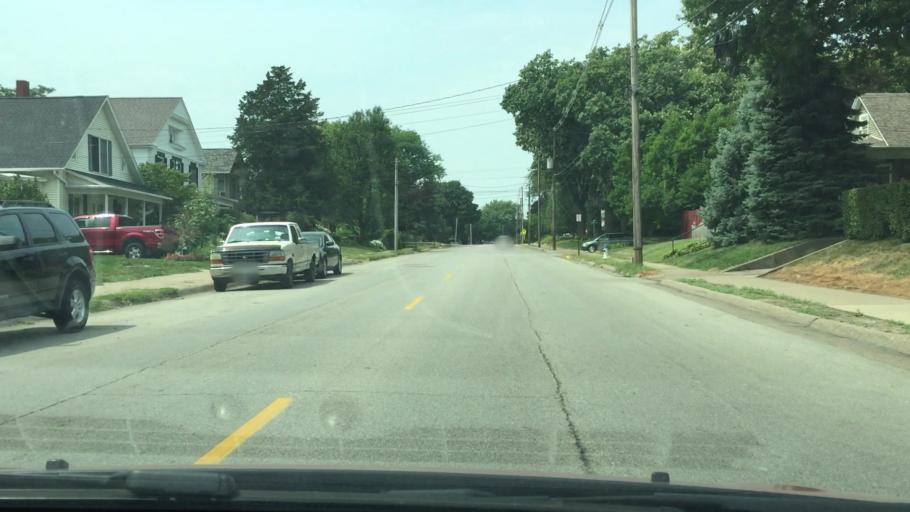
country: US
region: Iowa
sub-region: Muscatine County
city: Muscatine
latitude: 41.4366
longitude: -91.0554
